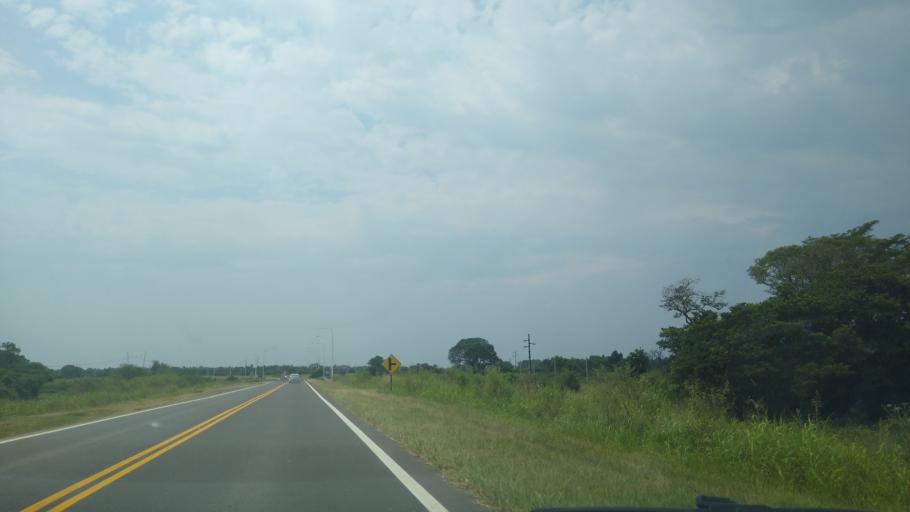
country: AR
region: Chaco
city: Margarita Belen
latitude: -27.0919
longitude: -58.9594
